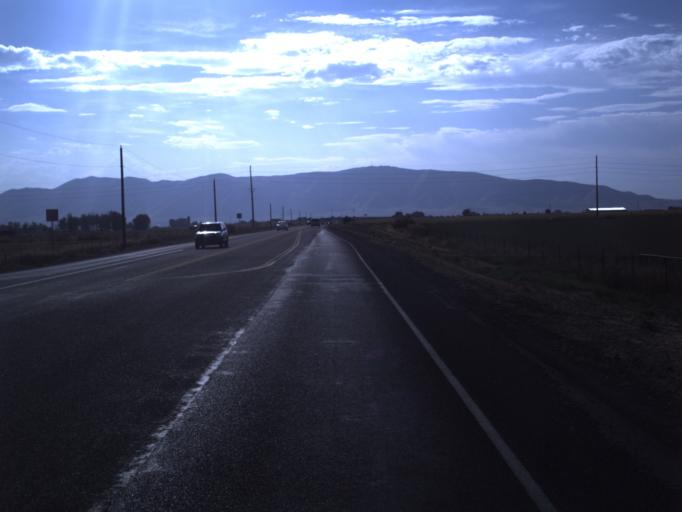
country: US
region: Utah
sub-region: Utah County
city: Salem
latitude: 40.0854
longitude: -111.6857
